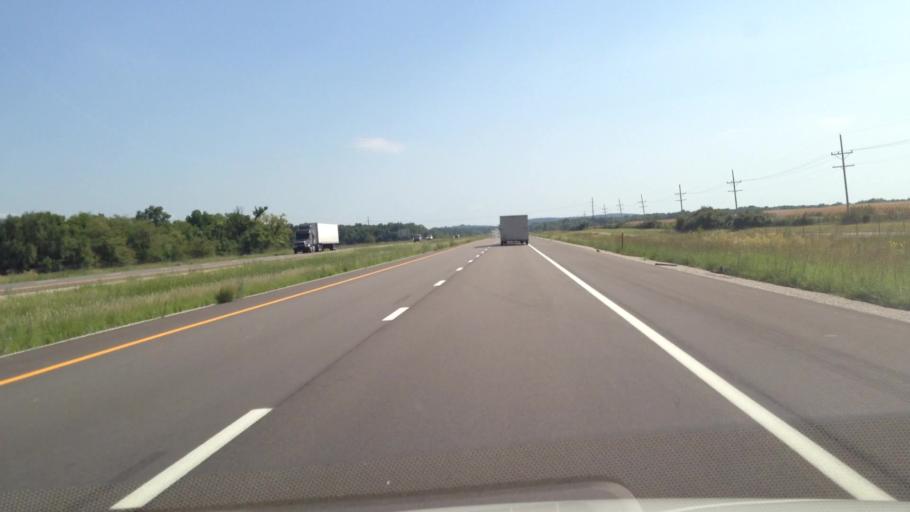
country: US
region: Kansas
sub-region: Linn County
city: La Cygne
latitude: 38.3290
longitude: -94.6777
